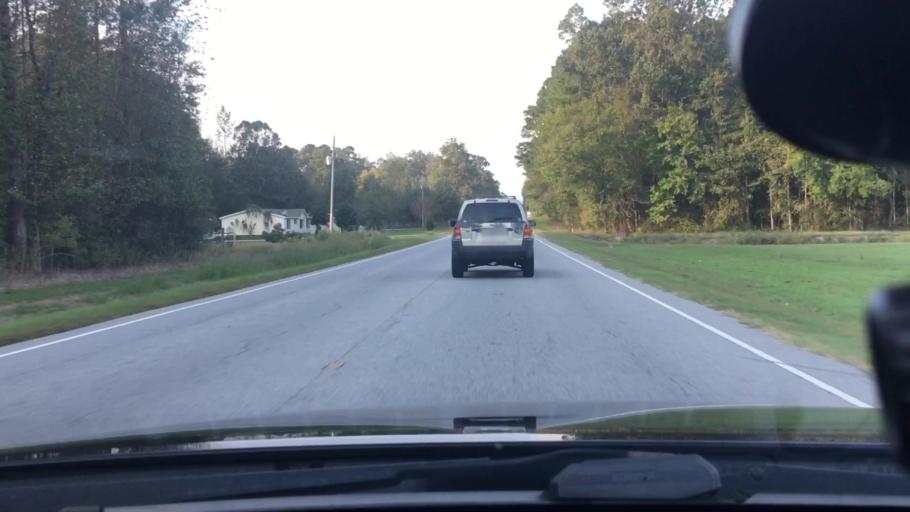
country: US
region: North Carolina
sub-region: Pitt County
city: Windsor
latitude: 35.4441
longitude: -77.2634
